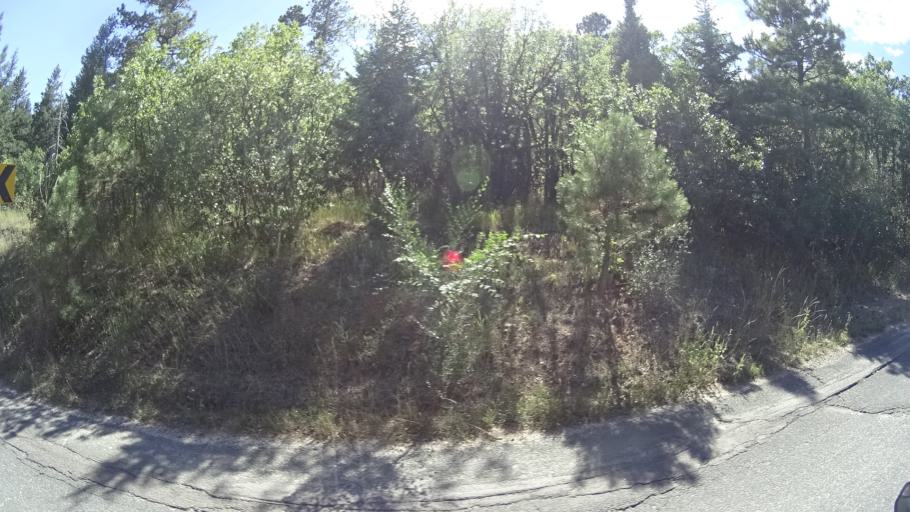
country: US
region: Colorado
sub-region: El Paso County
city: Manitou Springs
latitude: 38.8129
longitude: -104.8797
